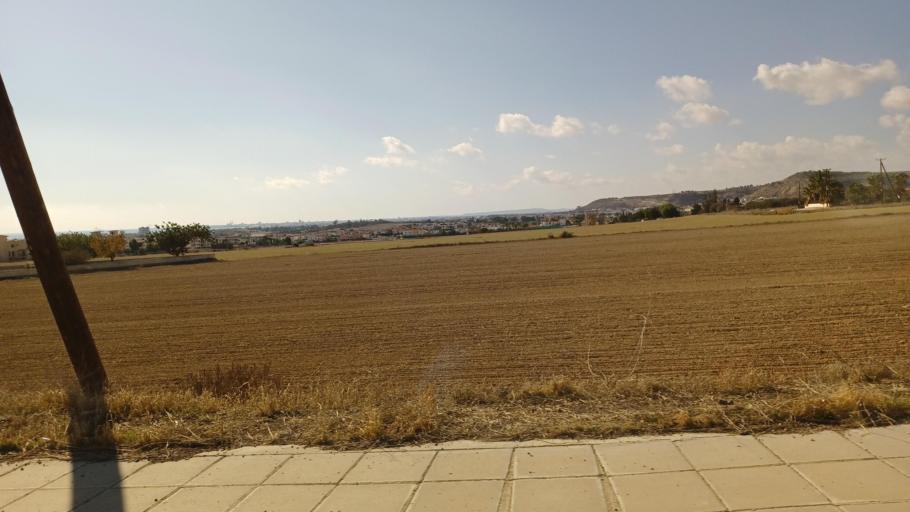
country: CY
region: Larnaka
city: Pyla
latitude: 35.0014
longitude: 33.6799
